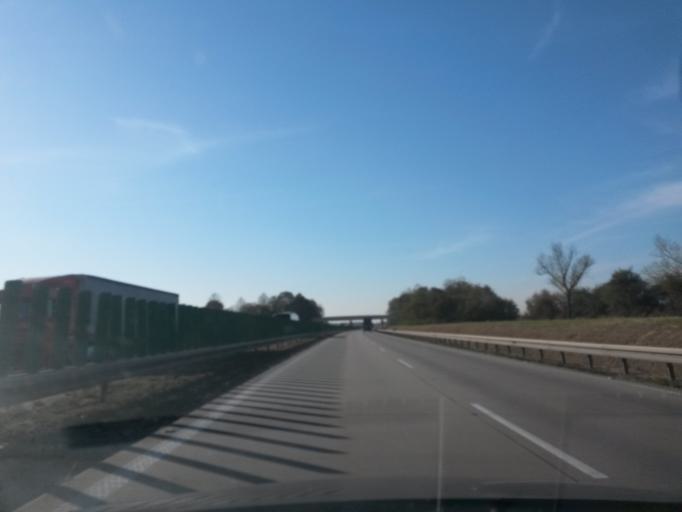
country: PL
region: Lower Silesian Voivodeship
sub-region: Powiat sredzki
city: Ciechow
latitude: 51.0507
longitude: 16.5591
